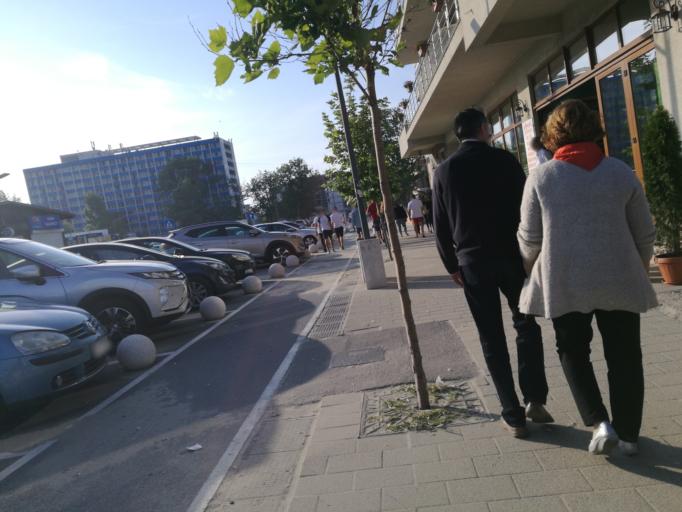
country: RO
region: Constanta
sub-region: Municipiul Constanta
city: Palazu Mare
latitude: 44.2258
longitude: 28.6308
